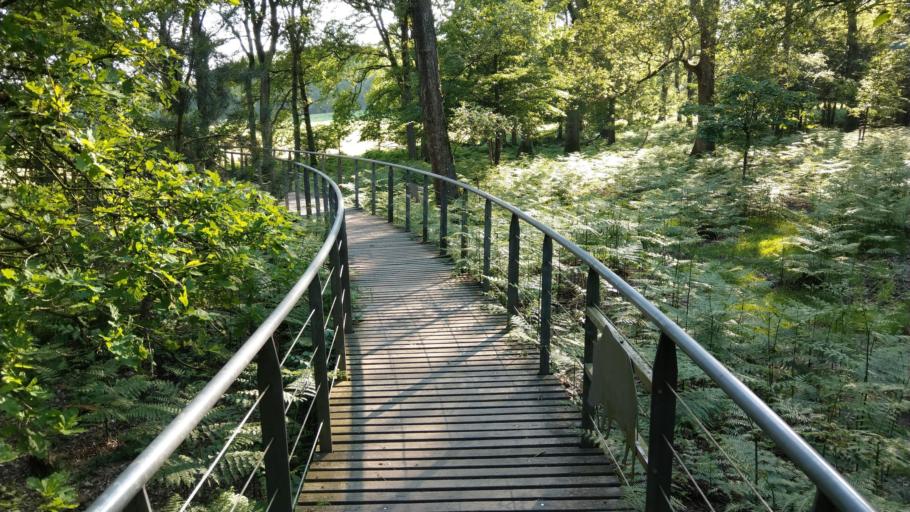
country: NL
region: Gelderland
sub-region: Gemeente Rheden
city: Rheden
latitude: 52.0210
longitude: 6.0062
